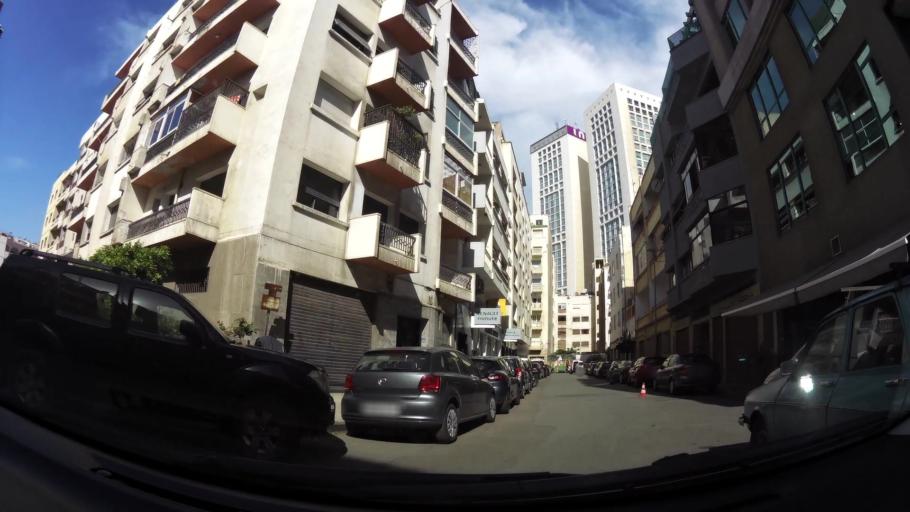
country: MA
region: Grand Casablanca
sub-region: Casablanca
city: Casablanca
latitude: 33.5856
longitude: -7.6307
